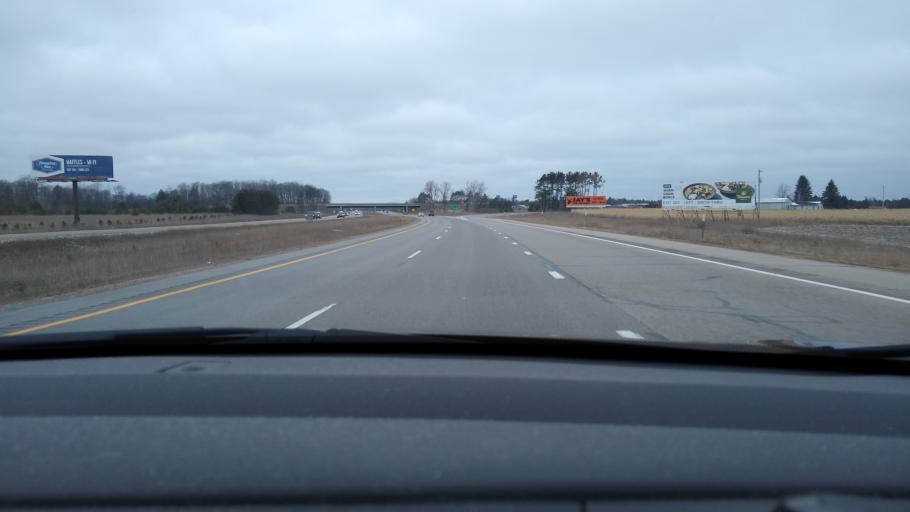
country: US
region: Michigan
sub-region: Otsego County
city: Gaylord
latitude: 44.9840
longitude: -84.6727
